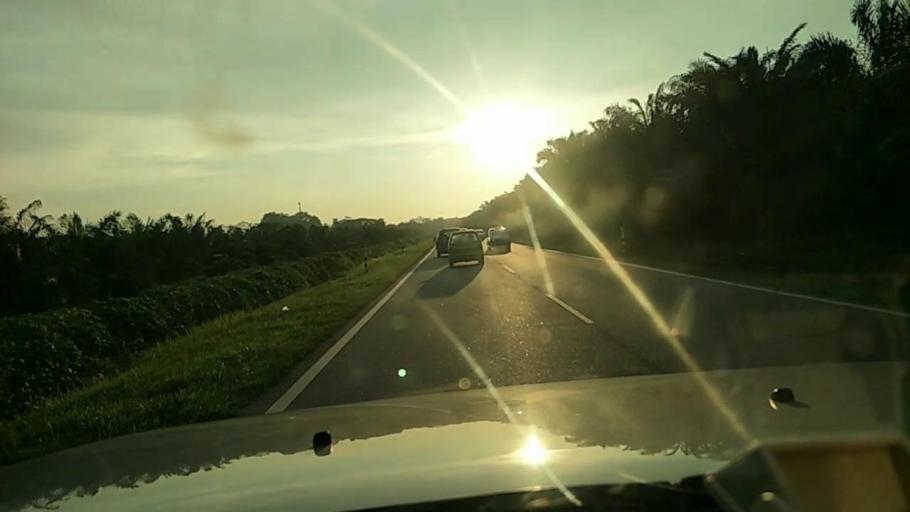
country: MY
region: Selangor
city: Kuala Selangor
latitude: 3.3089
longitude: 101.3255
